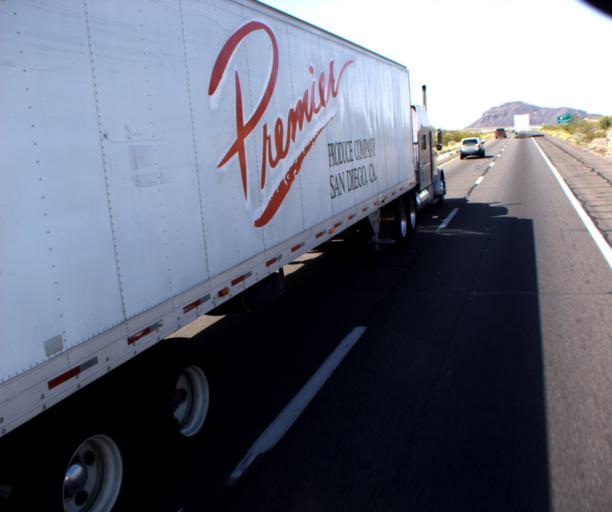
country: US
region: Arizona
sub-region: La Paz County
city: Quartzsite
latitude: 33.6610
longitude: -114.0018
